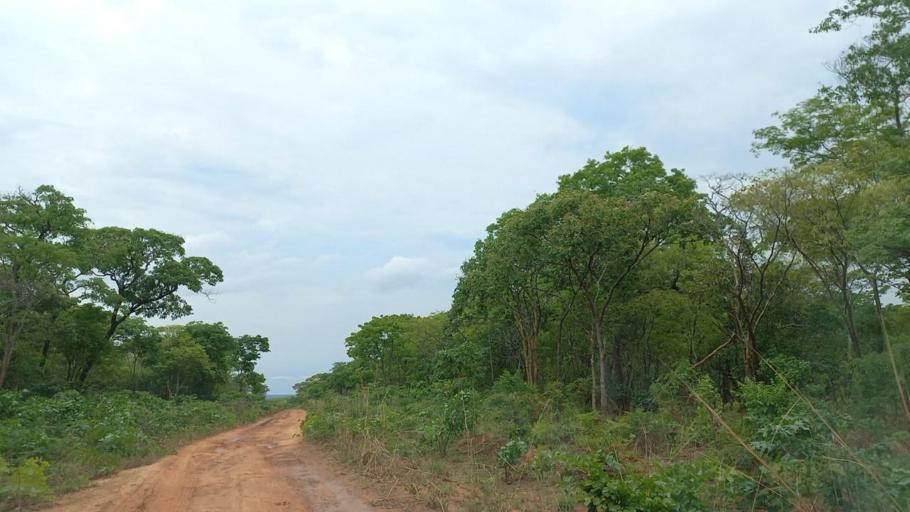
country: ZM
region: North-Western
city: Kalengwa
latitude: -13.6171
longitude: 24.9761
